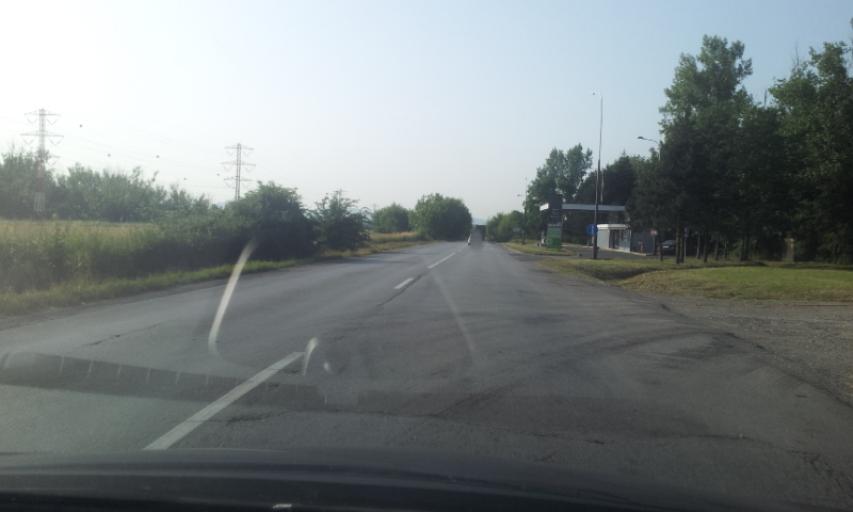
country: SK
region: Kosicky
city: Kosice
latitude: 48.6321
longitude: 21.2153
